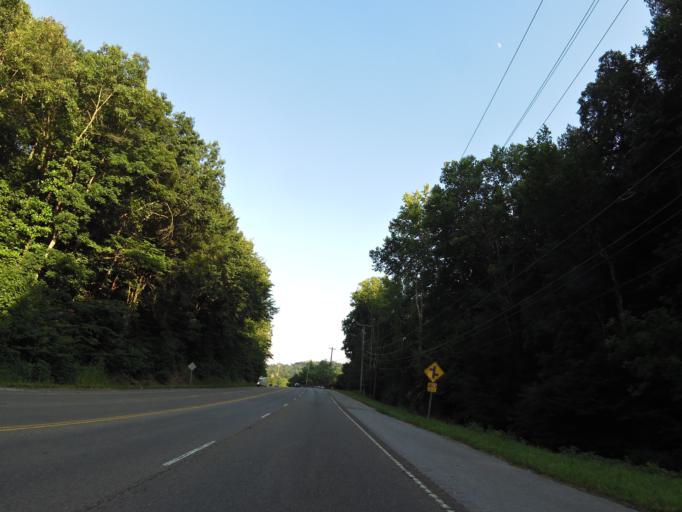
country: US
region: Tennessee
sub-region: Anderson County
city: Clinton
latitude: 36.0370
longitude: -84.1055
